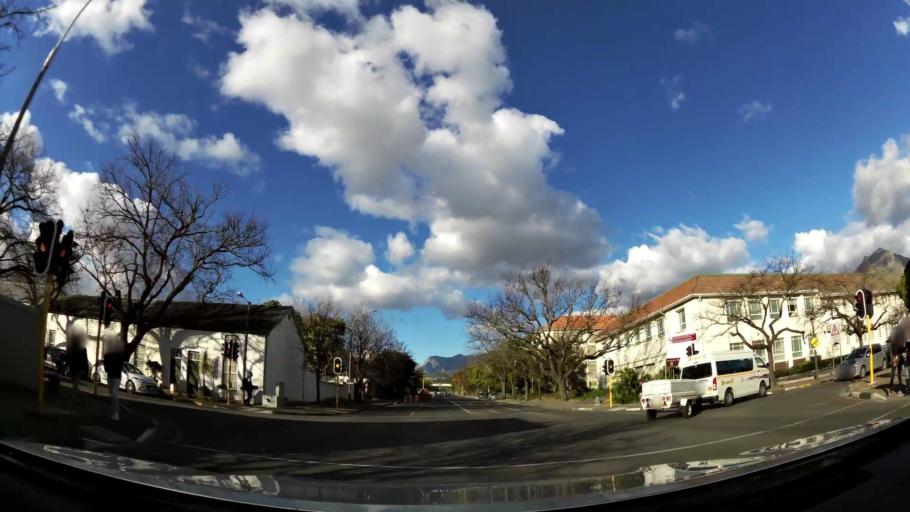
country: ZA
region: Western Cape
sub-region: Cape Winelands District Municipality
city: Stellenbosch
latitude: -33.9319
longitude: 18.8620
